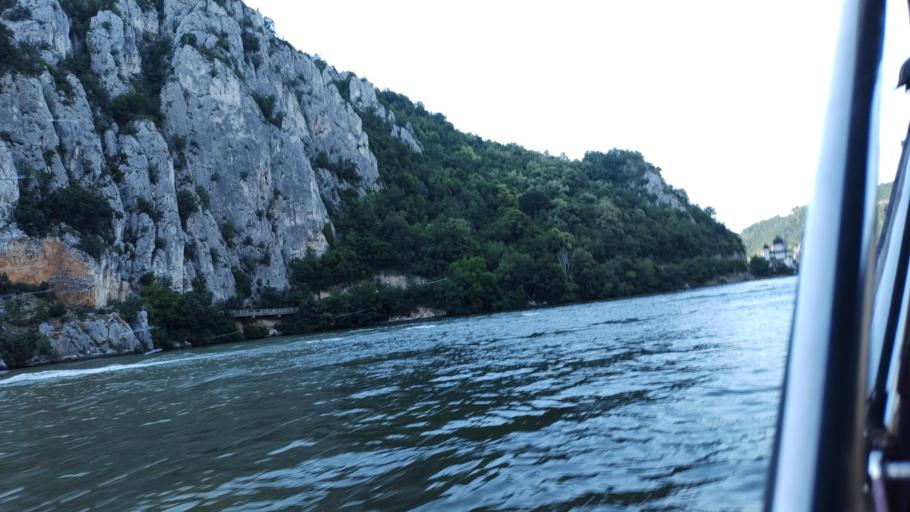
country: RO
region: Mehedinti
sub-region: Comuna Dubova
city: Dubova
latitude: 44.6344
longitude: 22.2906
